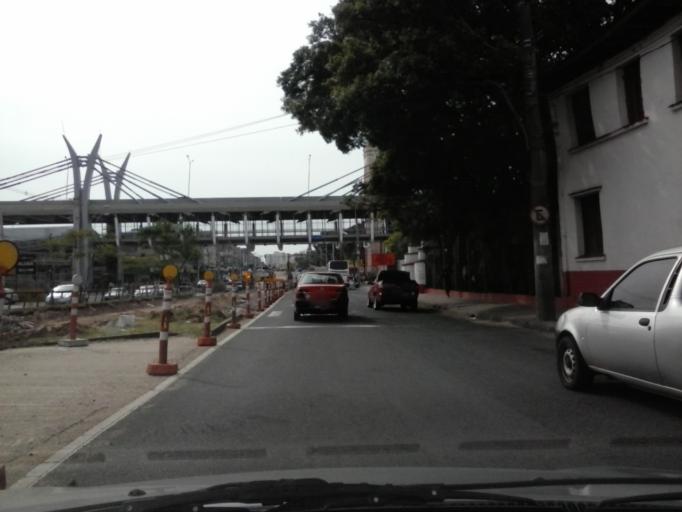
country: BR
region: Rio Grande do Sul
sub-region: Porto Alegre
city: Porto Alegre
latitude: -30.0639
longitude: -51.1845
